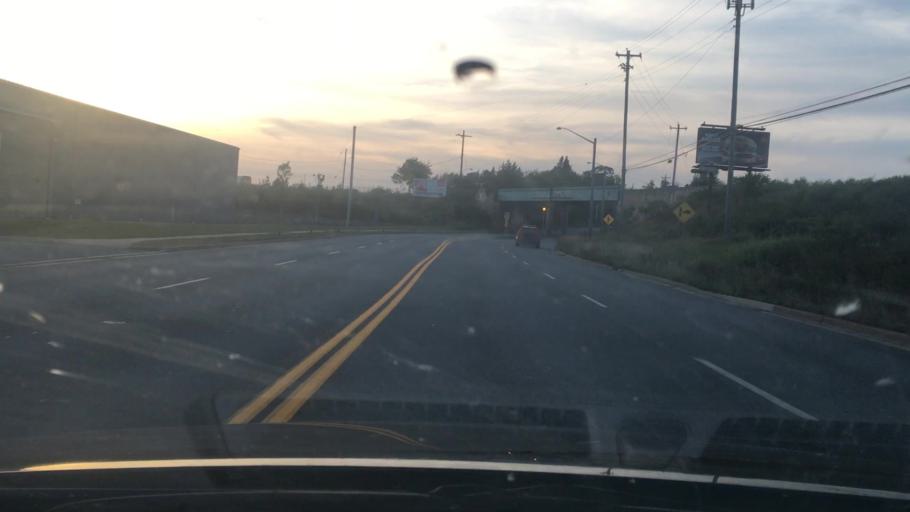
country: CA
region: Nova Scotia
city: Halifax
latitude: 44.6346
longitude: -63.5249
